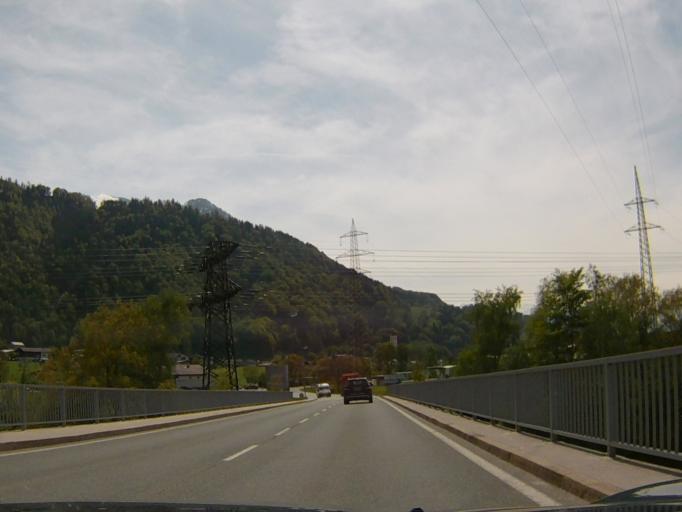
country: AT
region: Tyrol
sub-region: Politischer Bezirk Schwaz
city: Jenbach
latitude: 47.3846
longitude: 11.7738
